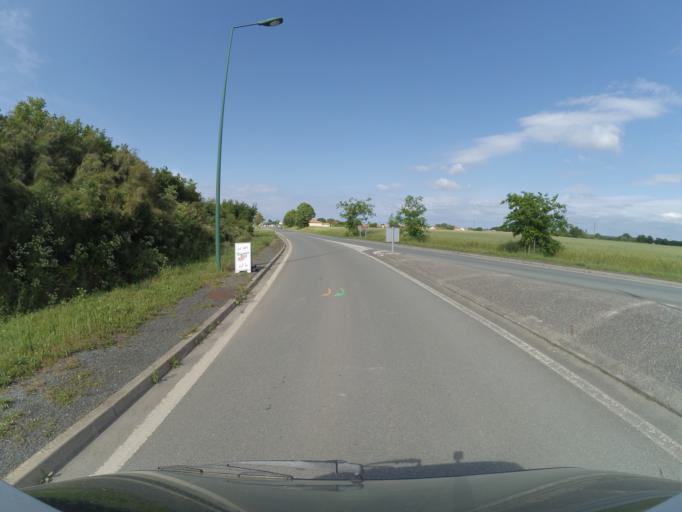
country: FR
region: Poitou-Charentes
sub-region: Departement de la Charente-Maritime
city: Saint-Xandre
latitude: 46.2348
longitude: -1.0736
